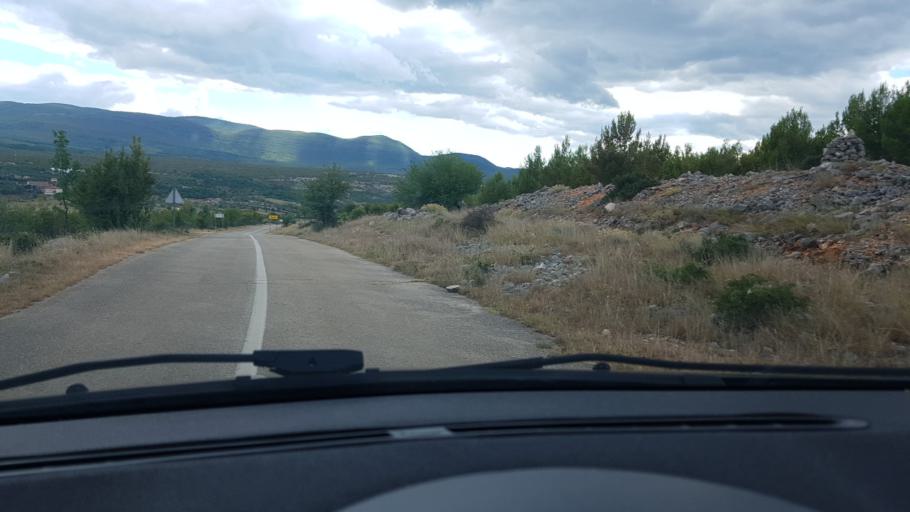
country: HR
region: Zadarska
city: Gracac
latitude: 44.1655
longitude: 15.8698
